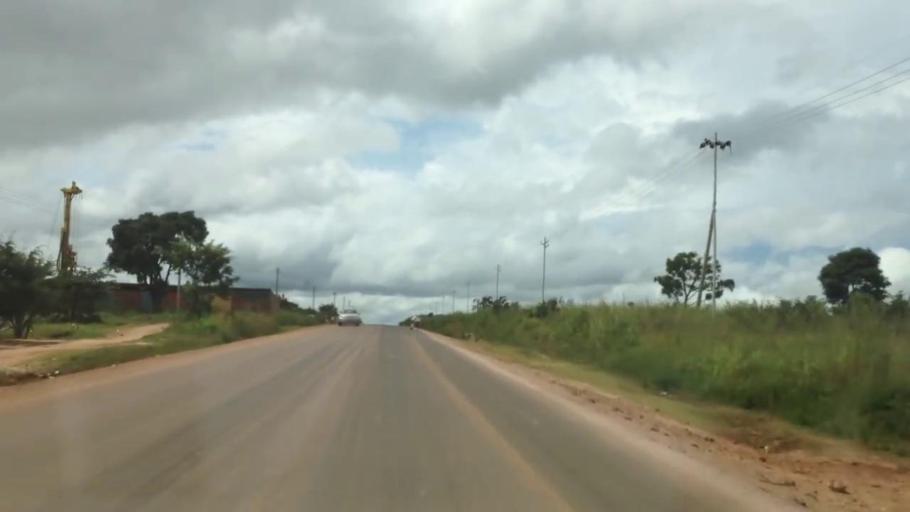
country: CD
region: Katanga
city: Kolwezi
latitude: -10.7428
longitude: 25.5129
